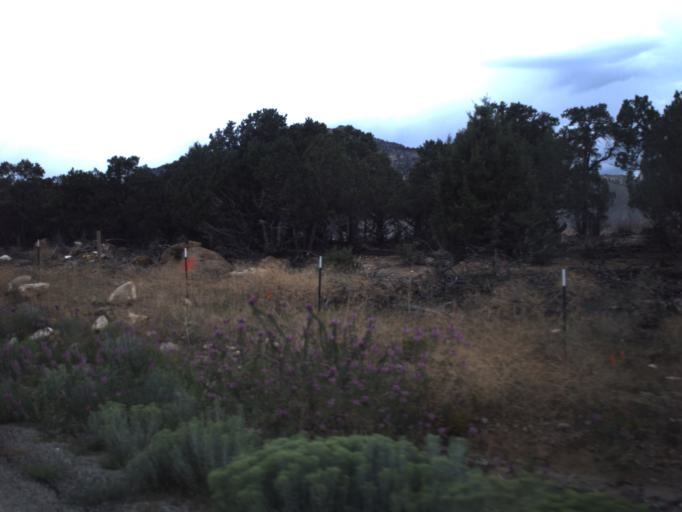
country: US
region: Utah
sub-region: Emery County
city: Huntington
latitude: 39.4842
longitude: -110.9868
